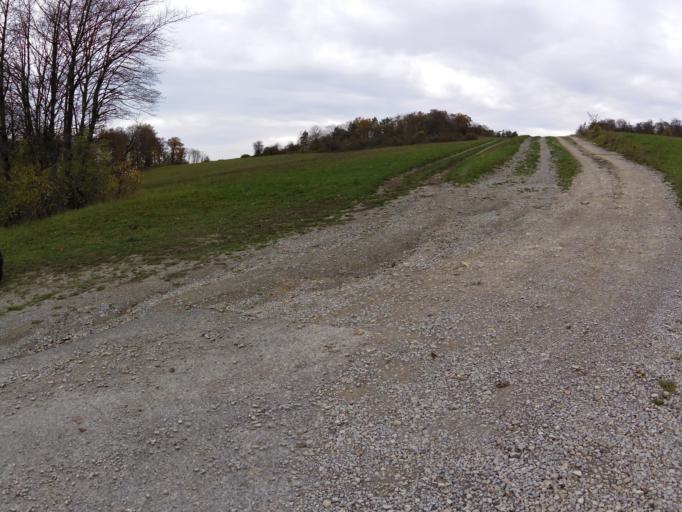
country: DE
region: Thuringia
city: Bischofroda
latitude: 51.0741
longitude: 10.3774
